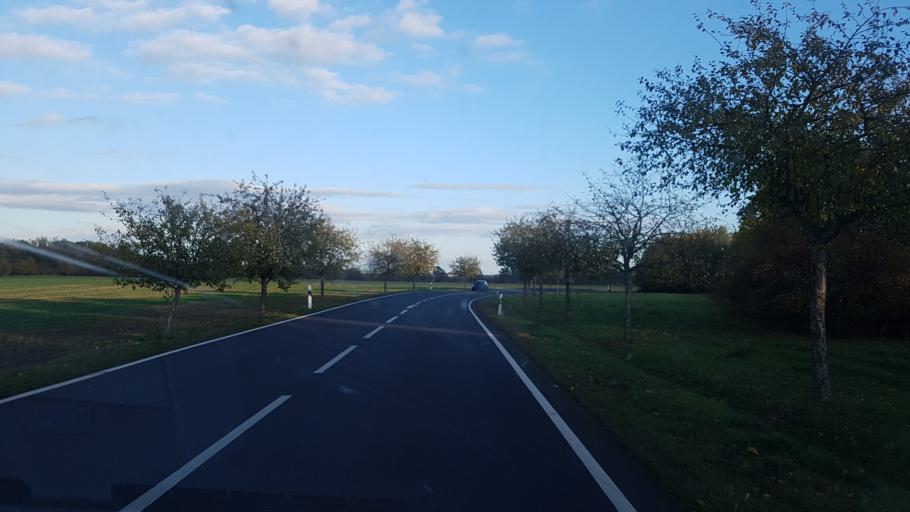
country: DE
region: Saxony
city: Dahlen
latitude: 51.3290
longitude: 13.0516
